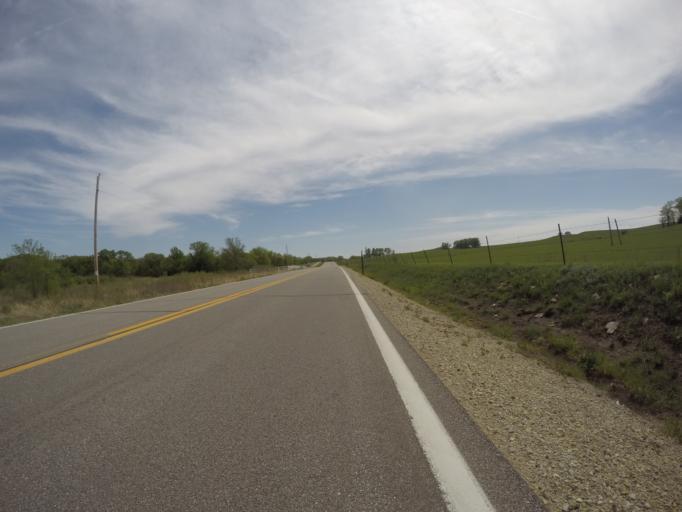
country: US
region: Kansas
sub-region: Riley County
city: Ogden
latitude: 39.0774
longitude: -96.6563
